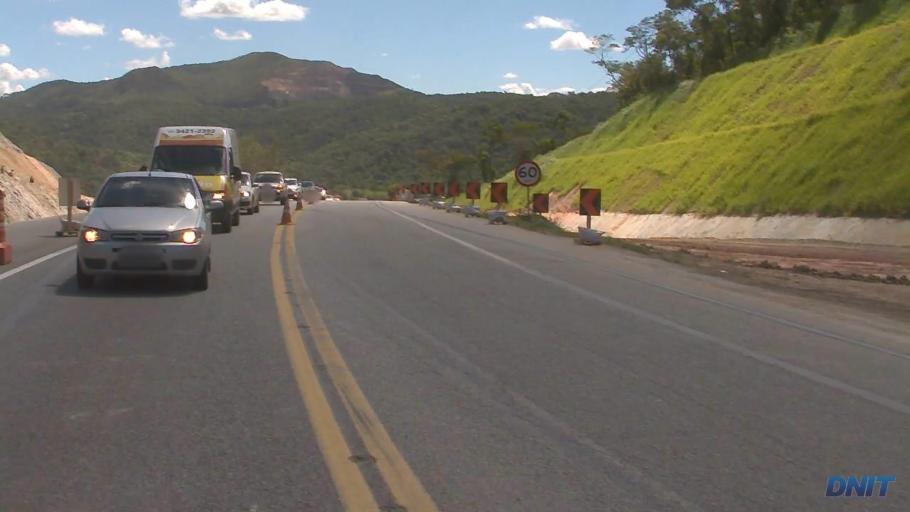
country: BR
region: Minas Gerais
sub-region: Caete
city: Caete
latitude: -19.7851
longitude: -43.6679
